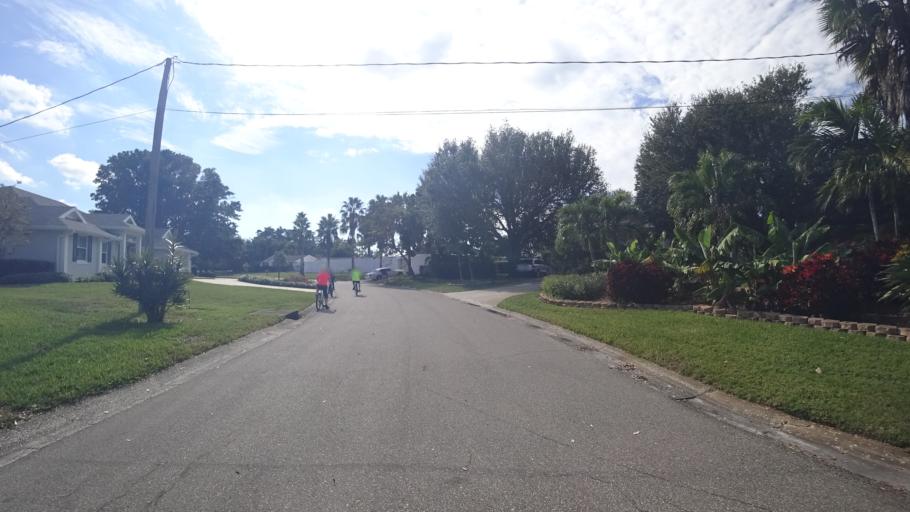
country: US
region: Florida
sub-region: Manatee County
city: West Bradenton
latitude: 27.5173
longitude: -82.6358
